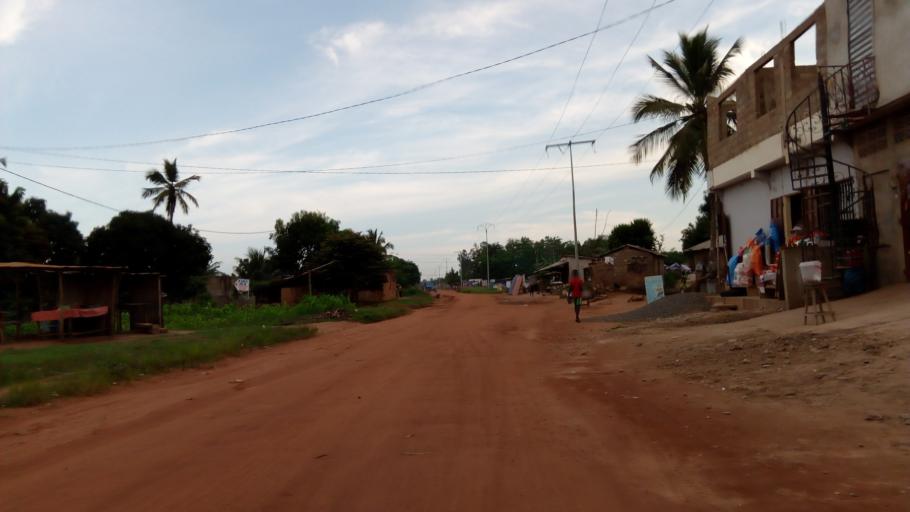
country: TG
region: Maritime
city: Lome
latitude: 6.2570
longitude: 1.1389
